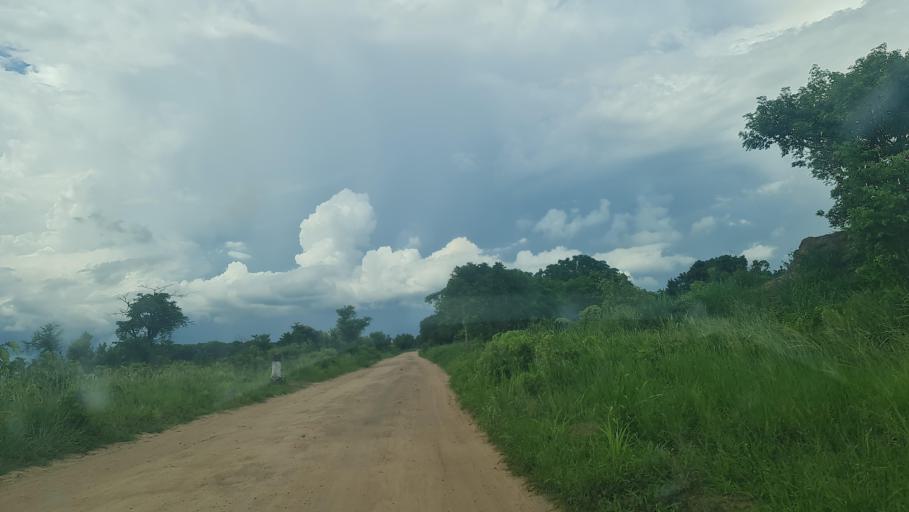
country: MW
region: Southern Region
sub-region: Nsanje District
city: Nsanje
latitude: -17.5958
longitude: 35.6748
